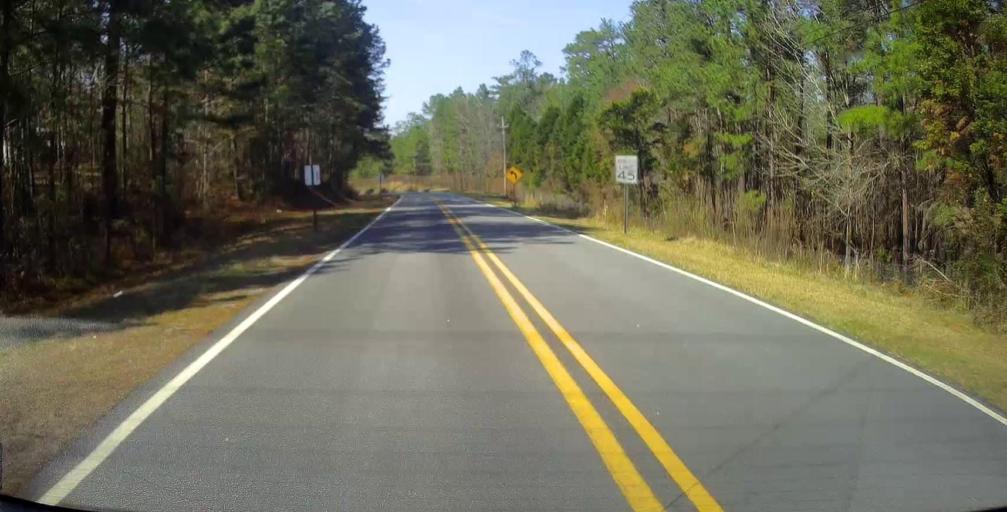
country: US
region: Georgia
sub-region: Bibb County
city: Macon
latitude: 32.9042
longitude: -83.6185
